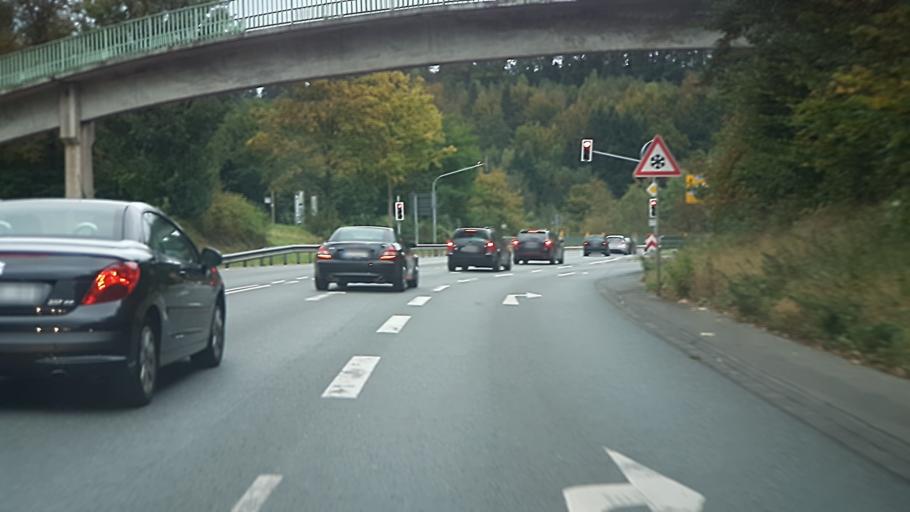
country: DE
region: North Rhine-Westphalia
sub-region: Regierungsbezirk Arnsberg
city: Attendorn
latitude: 51.1132
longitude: 7.8827
